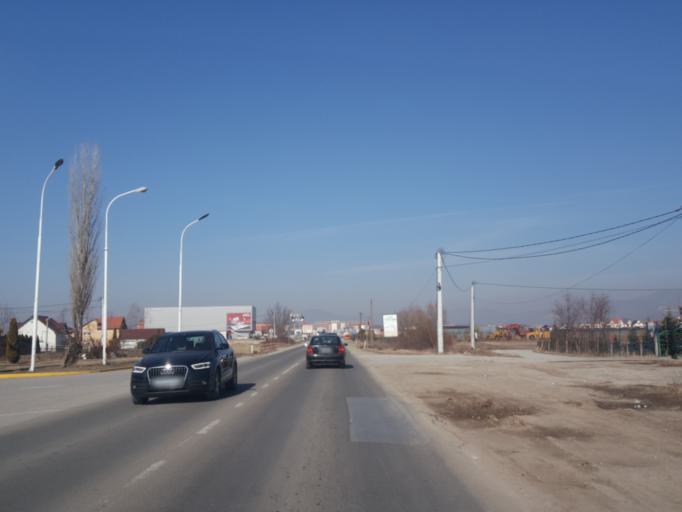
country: XK
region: Mitrovica
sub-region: Vushtrri
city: Vushtrri
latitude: 42.8092
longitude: 20.9879
